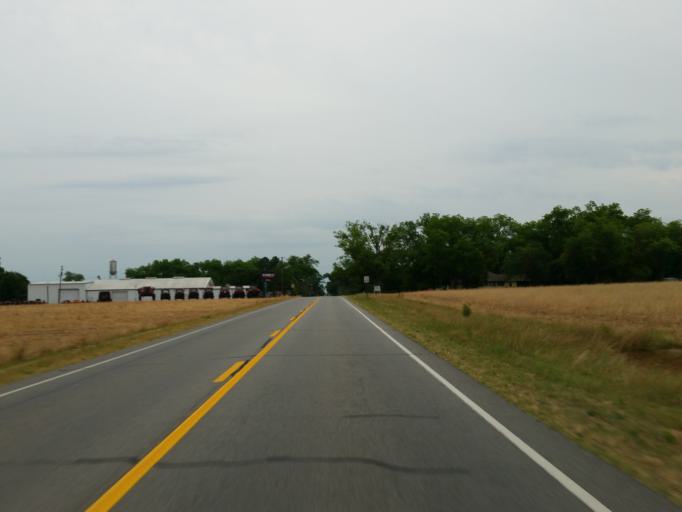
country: US
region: Georgia
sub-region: Dooly County
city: Unadilla
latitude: 32.2005
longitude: -83.7614
